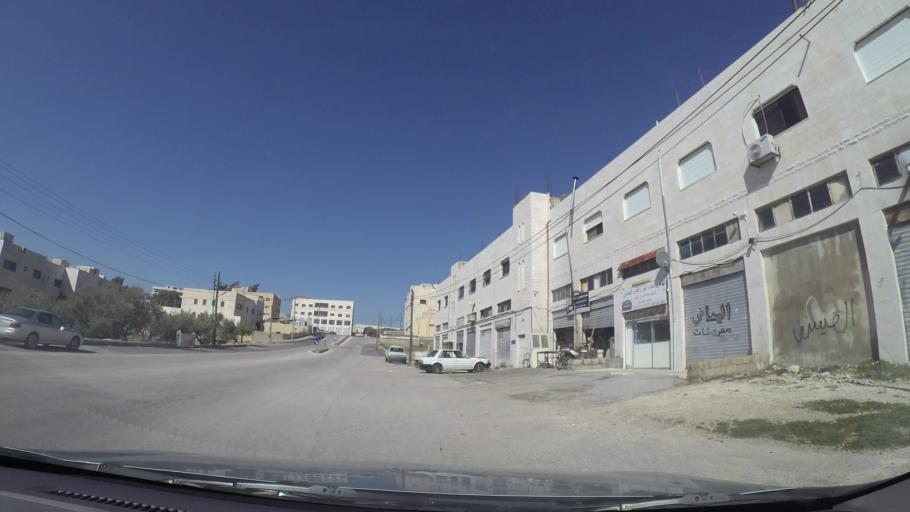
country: JO
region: Amman
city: Al Bunayyat ash Shamaliyah
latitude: 31.9068
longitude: 35.8974
